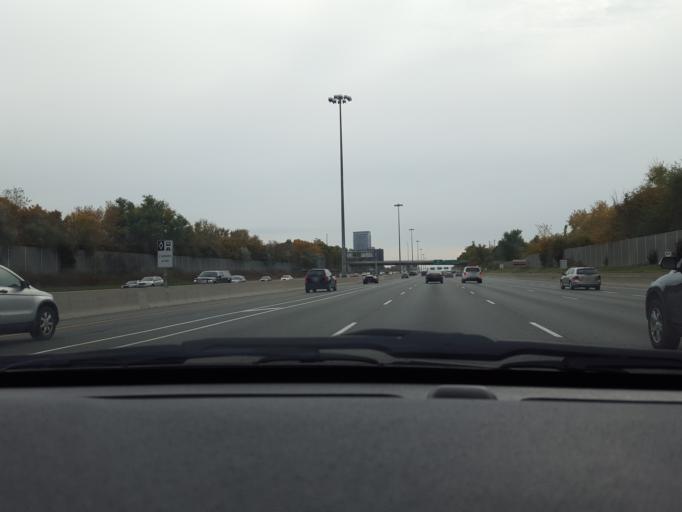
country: CA
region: Ontario
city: Willowdale
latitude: 43.7901
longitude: -79.3428
